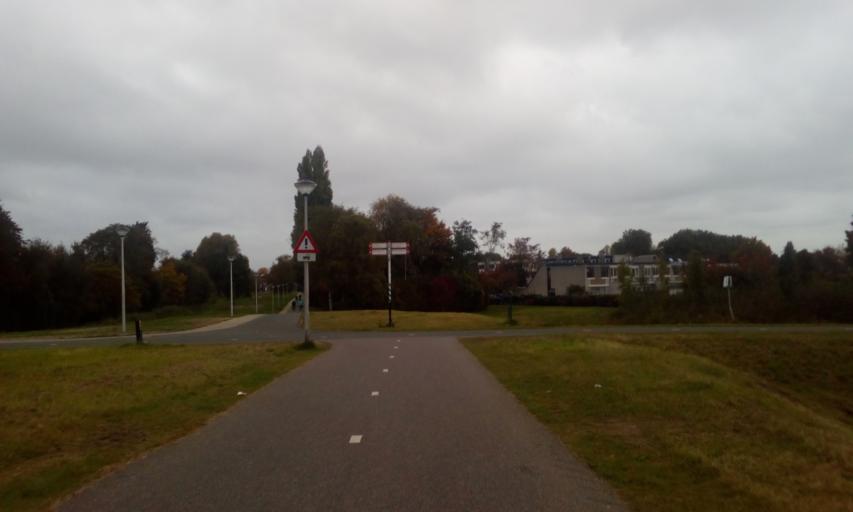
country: NL
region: South Holland
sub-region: Gemeente Lansingerland
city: Bergschenhoek
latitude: 52.0011
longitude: 4.4966
